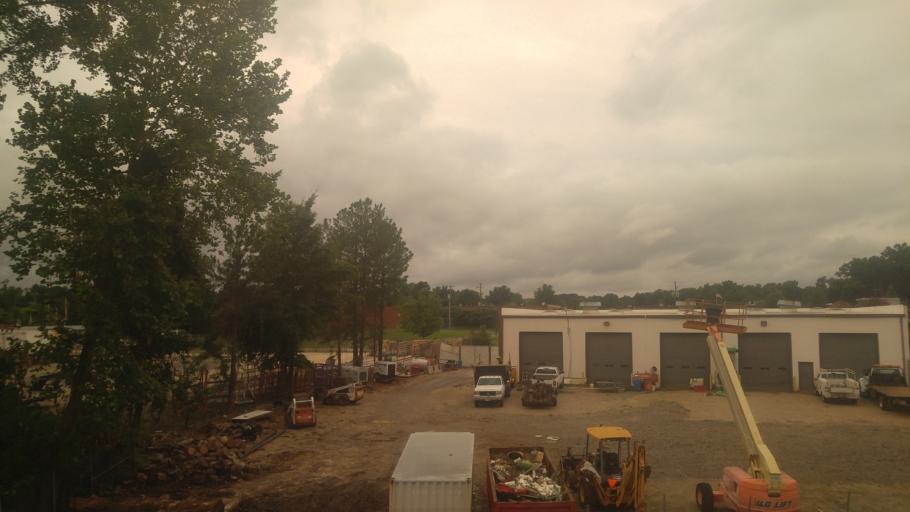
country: US
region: Virginia
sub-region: Henrico County
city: Laurel
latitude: 37.6243
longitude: -77.4992
